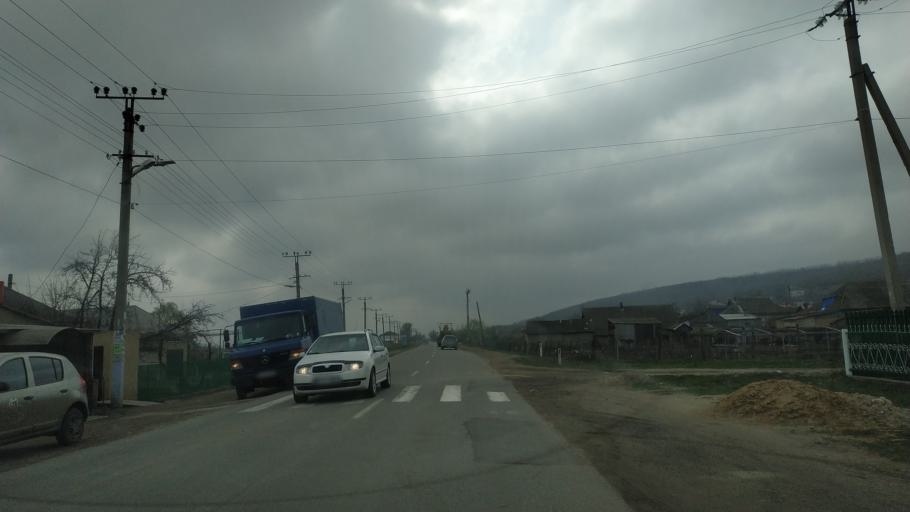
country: MD
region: Cimislia
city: Cimislia
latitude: 46.5107
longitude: 28.8027
